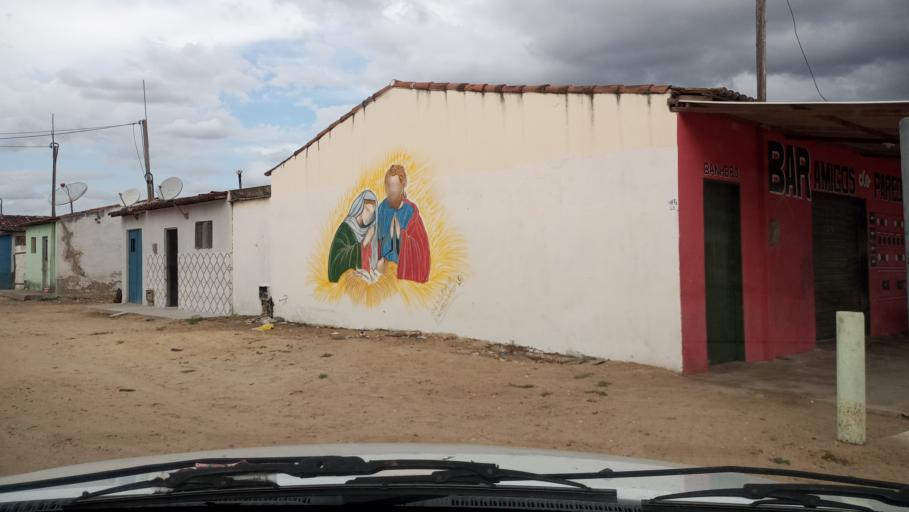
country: BR
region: Rio Grande do Norte
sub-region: Tangara
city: Tangara
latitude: -6.1920
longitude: -35.8000
